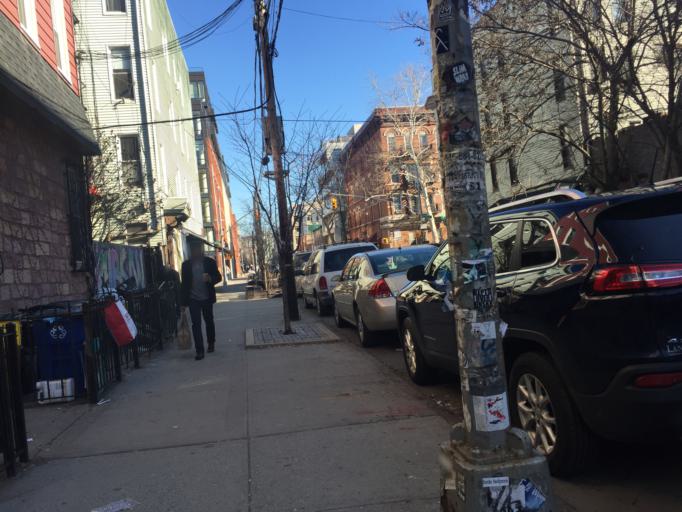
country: US
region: New York
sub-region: Queens County
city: Long Island City
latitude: 40.7203
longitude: -73.9560
